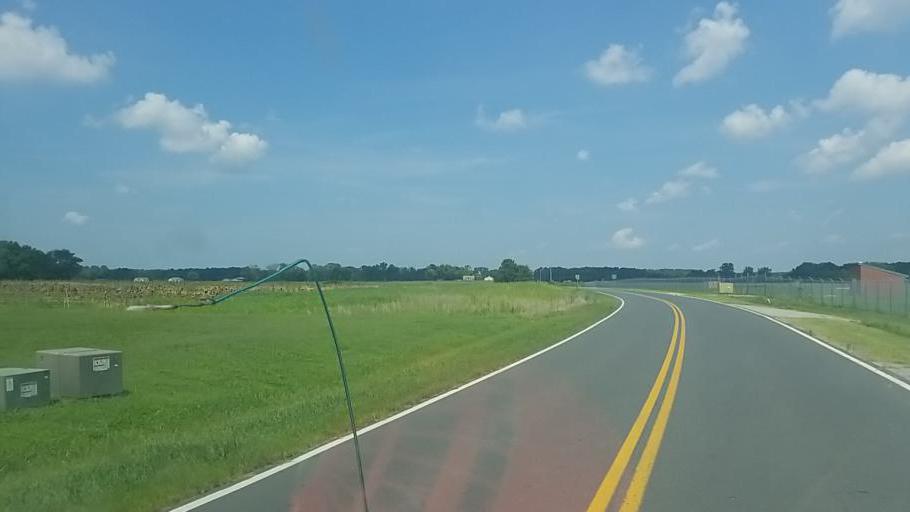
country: US
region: Maryland
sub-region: Wicomico County
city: Salisbury
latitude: 38.3450
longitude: -75.5192
